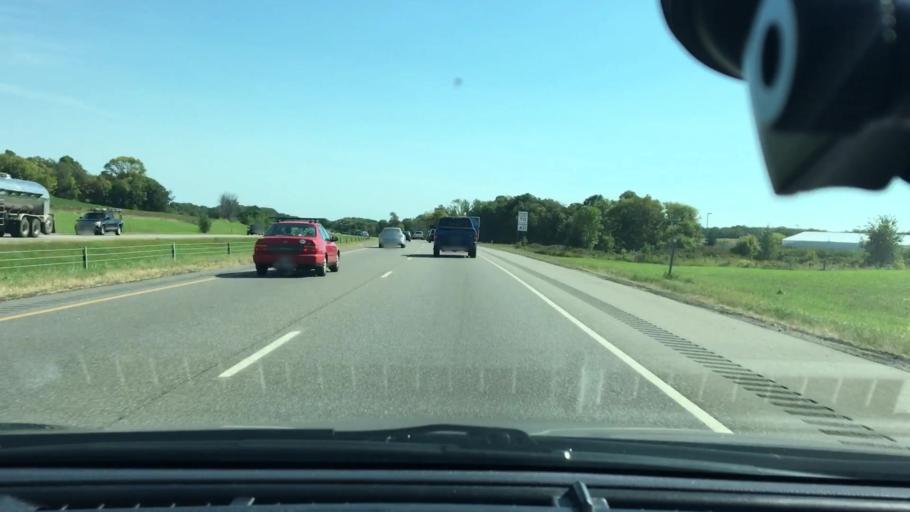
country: US
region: Minnesota
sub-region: Wright County
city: Albertville
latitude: 45.2322
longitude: -93.6392
